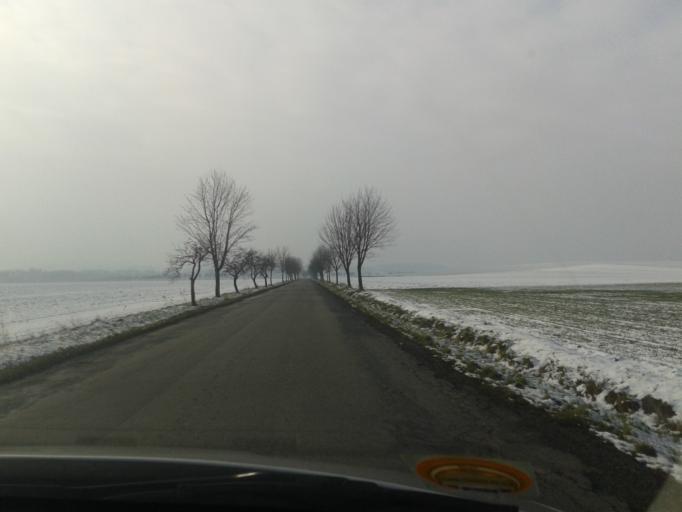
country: CZ
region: Olomoucky
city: Celechovice na Hane
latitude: 49.4904
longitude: 17.0796
